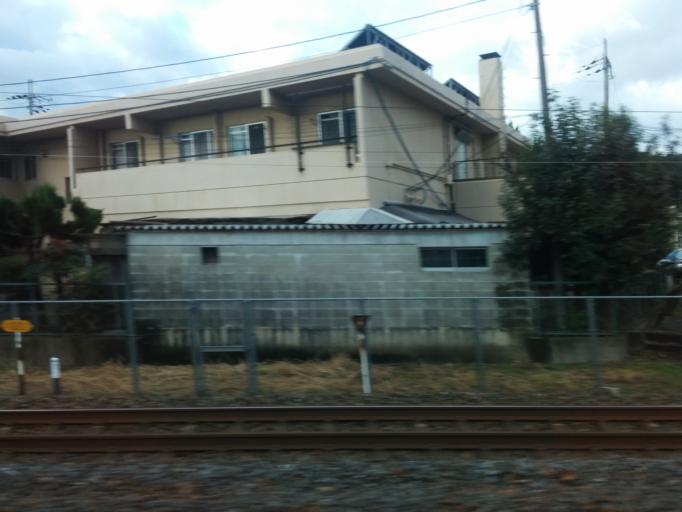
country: JP
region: Shiga Prefecture
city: Otsu-shi
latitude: 34.9894
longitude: 135.8884
